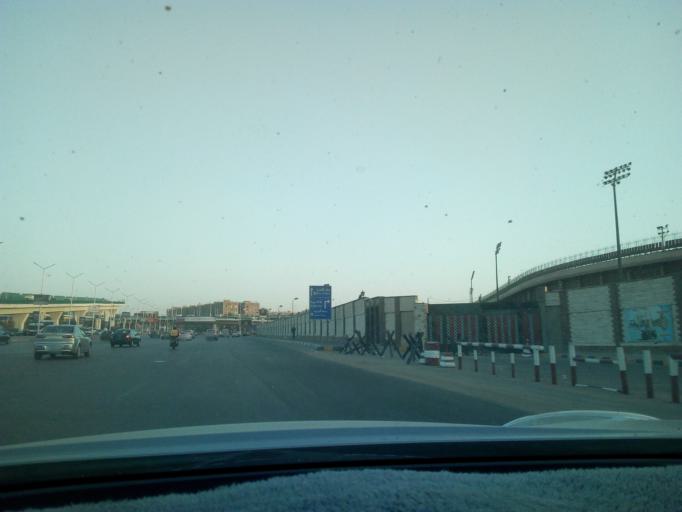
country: EG
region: Muhafazat al Qalyubiyah
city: Al Khankah
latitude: 30.1127
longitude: 31.3680
